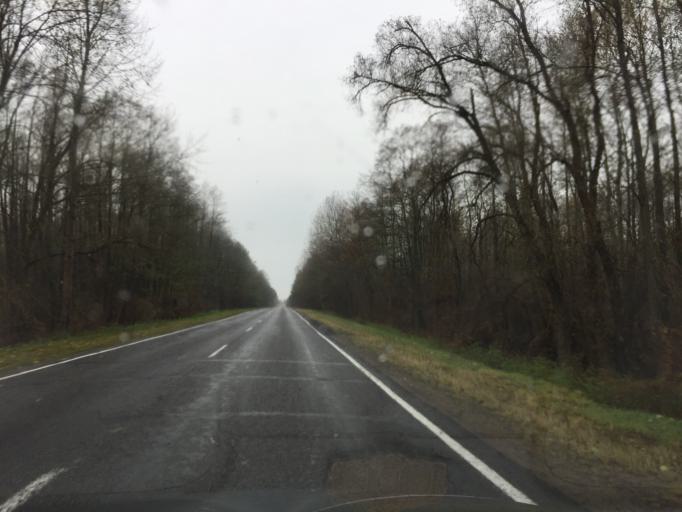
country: BY
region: Gomel
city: Karma
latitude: 53.3176
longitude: 30.7563
